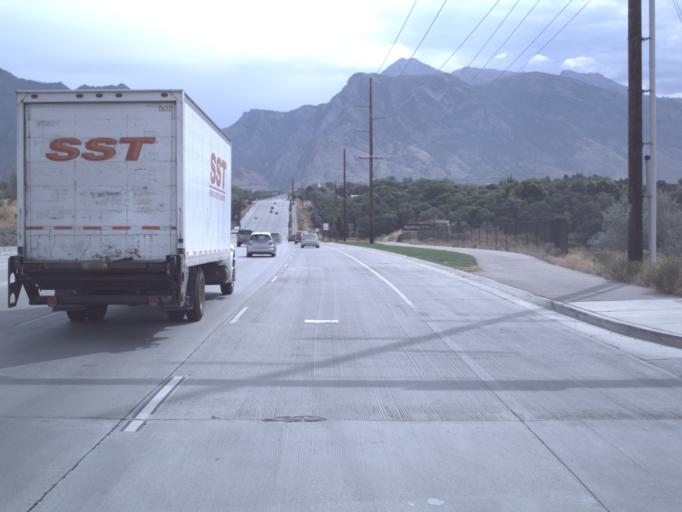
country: US
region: Utah
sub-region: Utah County
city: Alpine
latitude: 40.4316
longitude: -111.8216
